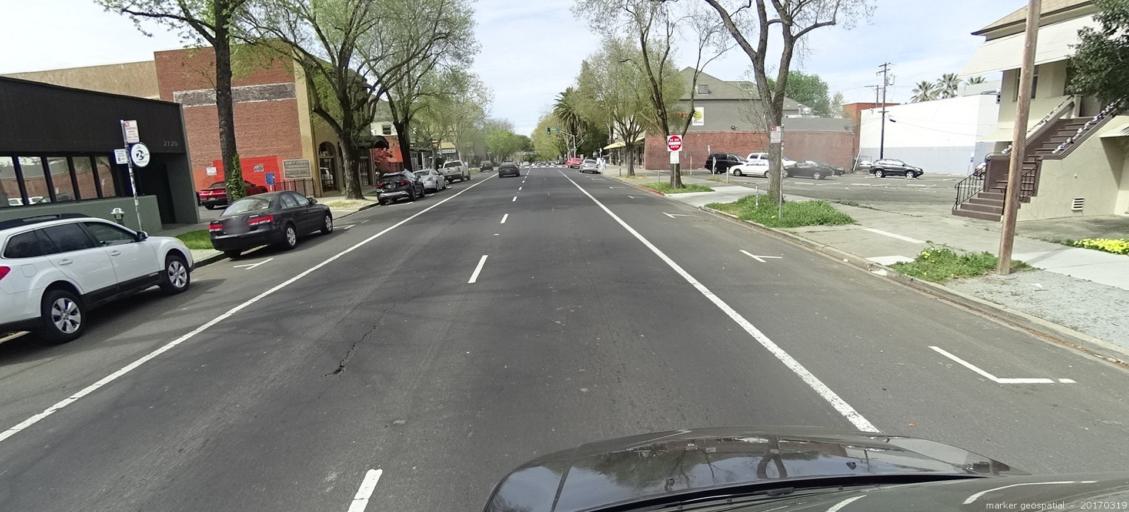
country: US
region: California
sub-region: Sacramento County
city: Sacramento
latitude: 38.5694
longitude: -121.4803
